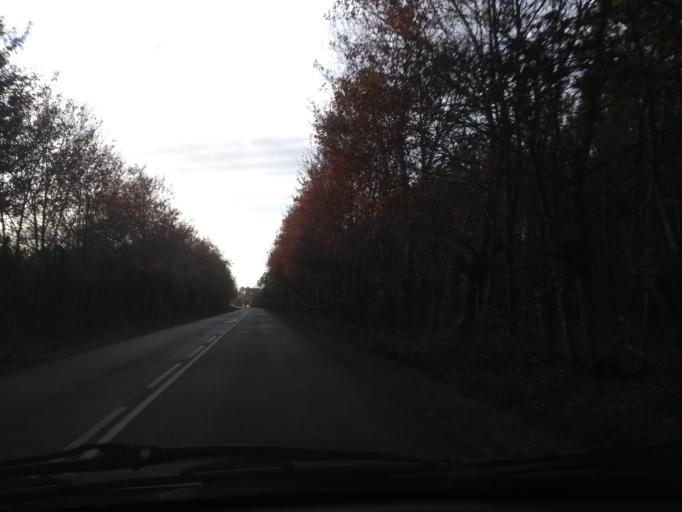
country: FR
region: Aquitaine
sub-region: Departement de la Gironde
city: Le Barp
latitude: 44.5934
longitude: -0.7235
